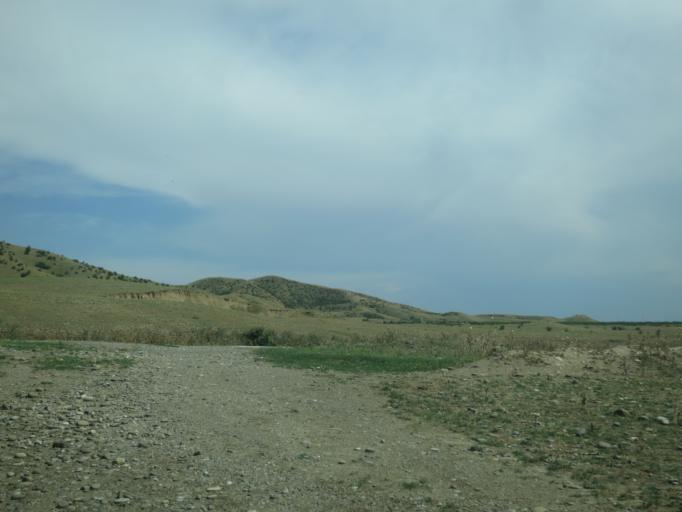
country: GE
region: Kvemo Kartli
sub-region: Gardabani
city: Gardabani
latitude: 41.4969
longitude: 45.1886
